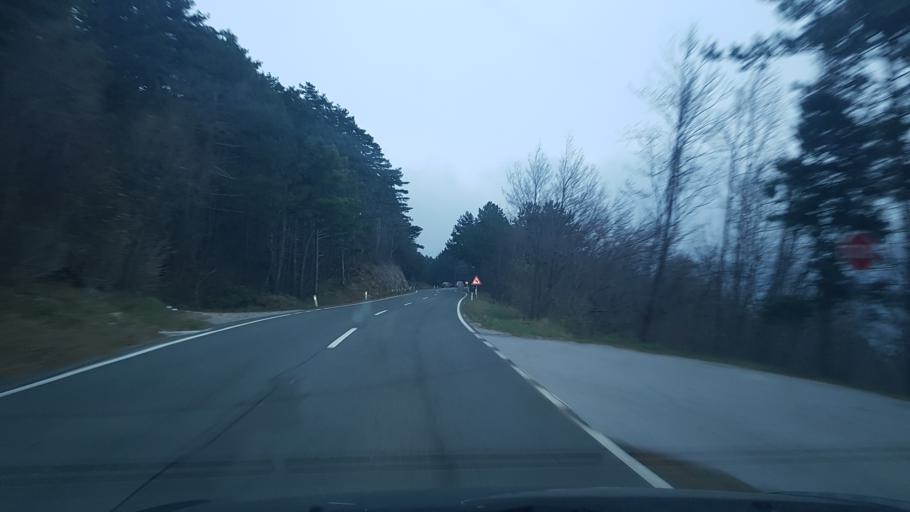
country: SI
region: Vipava
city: Vipava
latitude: 45.8806
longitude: 13.9522
